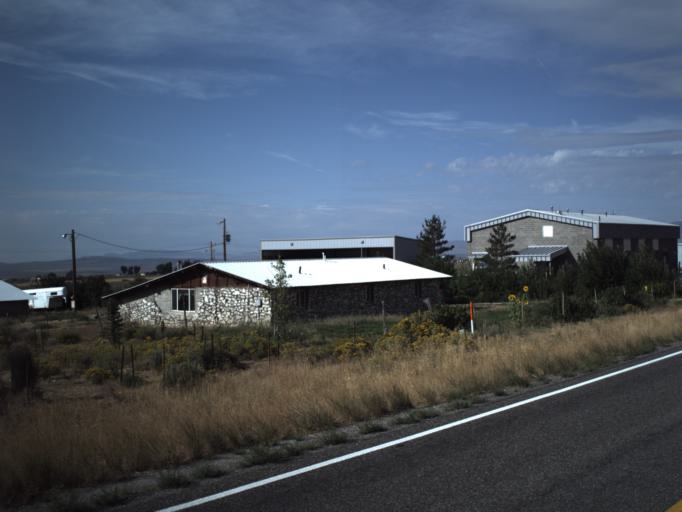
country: US
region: Idaho
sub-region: Cassia County
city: Burley
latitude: 41.8170
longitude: -113.3316
